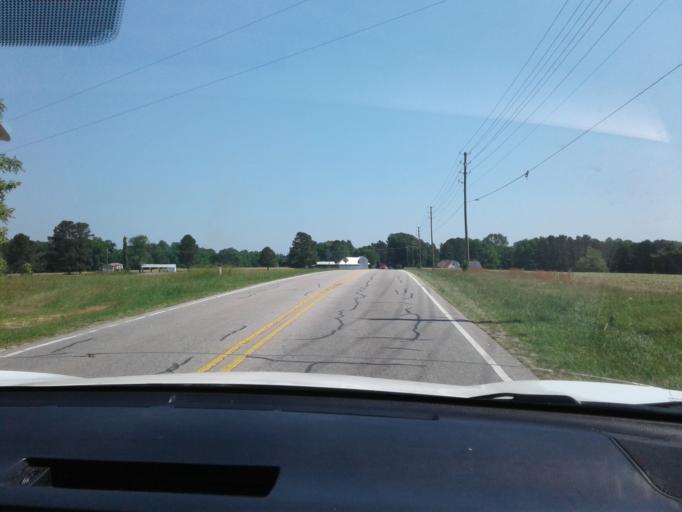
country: US
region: North Carolina
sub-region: Wake County
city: Fuquay-Varina
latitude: 35.5862
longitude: -78.8401
